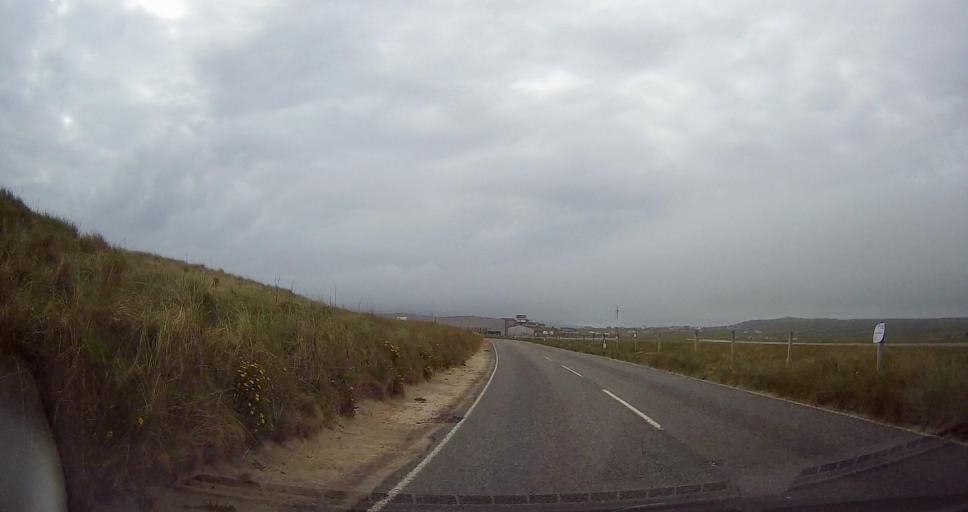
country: GB
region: Scotland
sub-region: Shetland Islands
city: Sandwick
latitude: 59.8750
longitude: -1.2923
